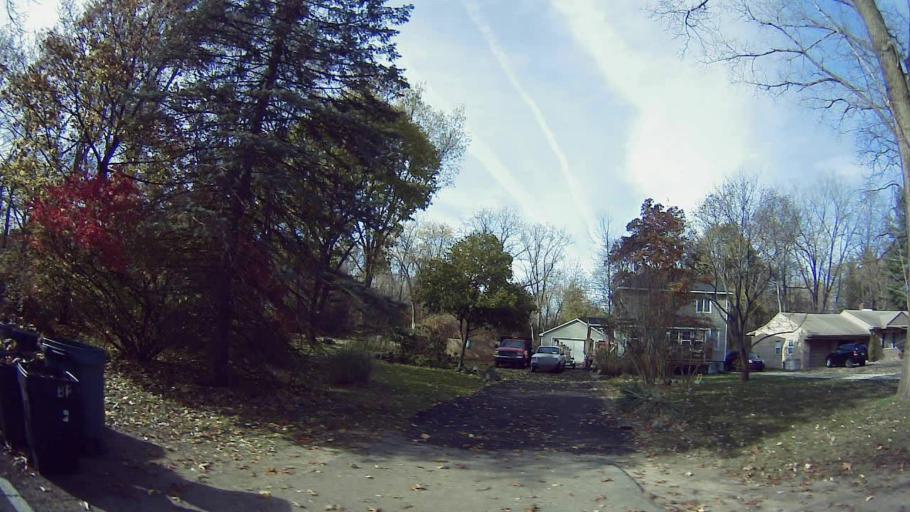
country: US
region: Michigan
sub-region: Oakland County
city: Southfield
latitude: 42.4471
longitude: -83.2698
